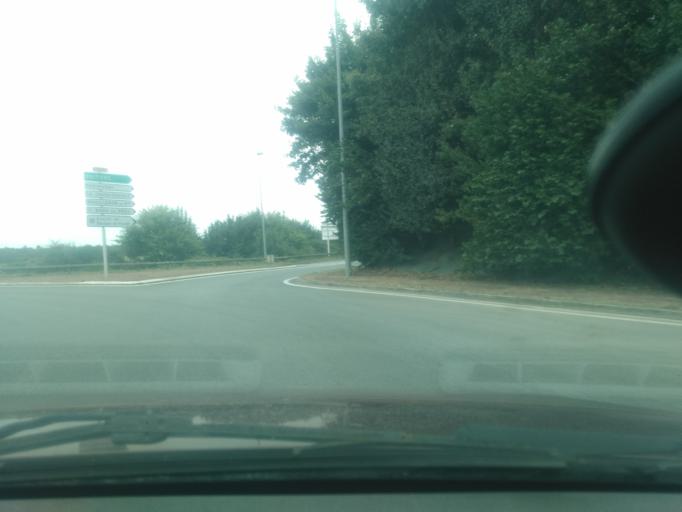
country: FR
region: Pays de la Loire
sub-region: Departement de la Vendee
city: Chantonnay
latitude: 46.6845
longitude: -1.0367
